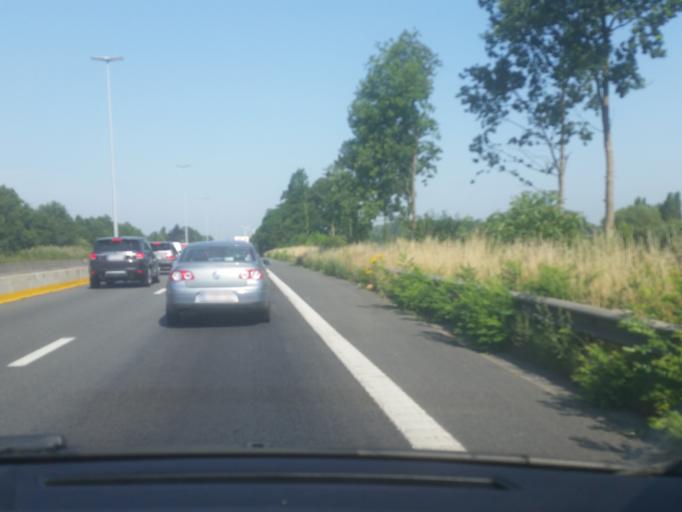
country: BE
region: Flanders
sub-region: Provincie Oost-Vlaanderen
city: Sint-Lievens-Houtem
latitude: 50.9622
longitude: 3.8615
